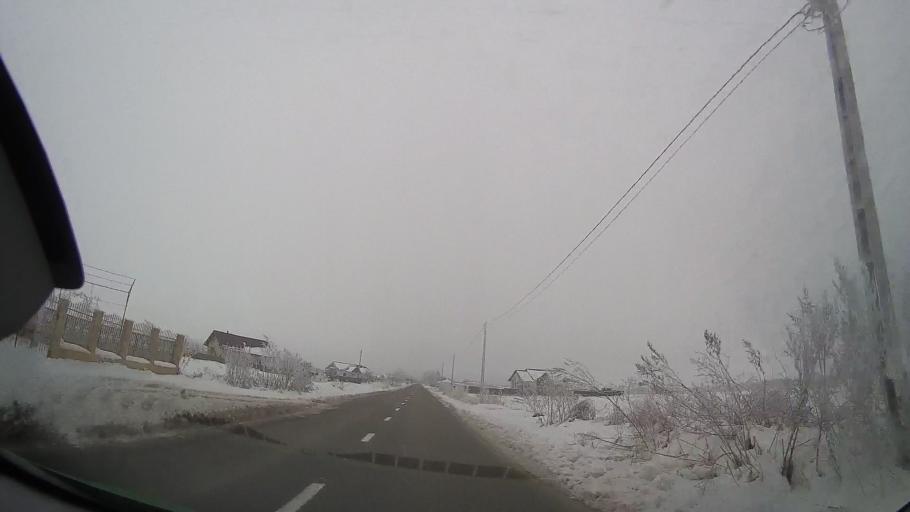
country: RO
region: Neamt
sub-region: Comuna Horia
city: Cotu Vames
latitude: 46.8932
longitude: 26.9625
